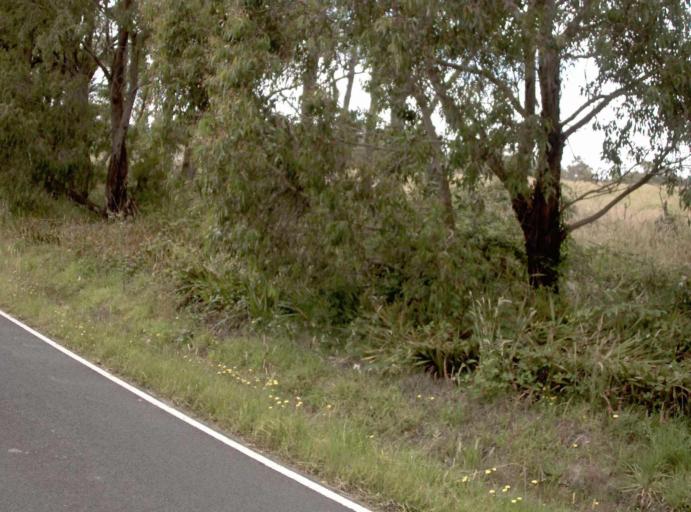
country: AU
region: Victoria
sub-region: Cardinia
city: Koo-Wee-Rup
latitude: -38.3400
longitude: 145.6693
